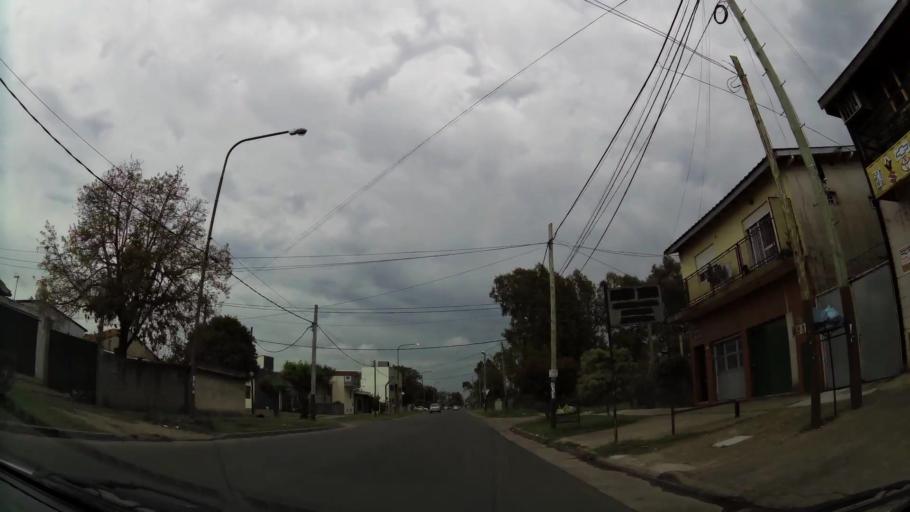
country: AR
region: Buenos Aires
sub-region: Partido de Quilmes
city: Quilmes
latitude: -34.7466
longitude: -58.2895
